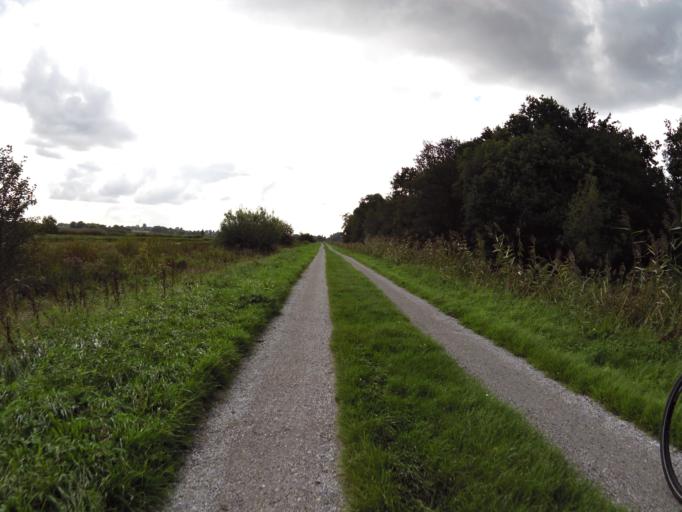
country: NL
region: North Holland
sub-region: Gemeente Wijdemeren
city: Nieuw-Loosdrecht
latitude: 52.1795
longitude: 5.1137
